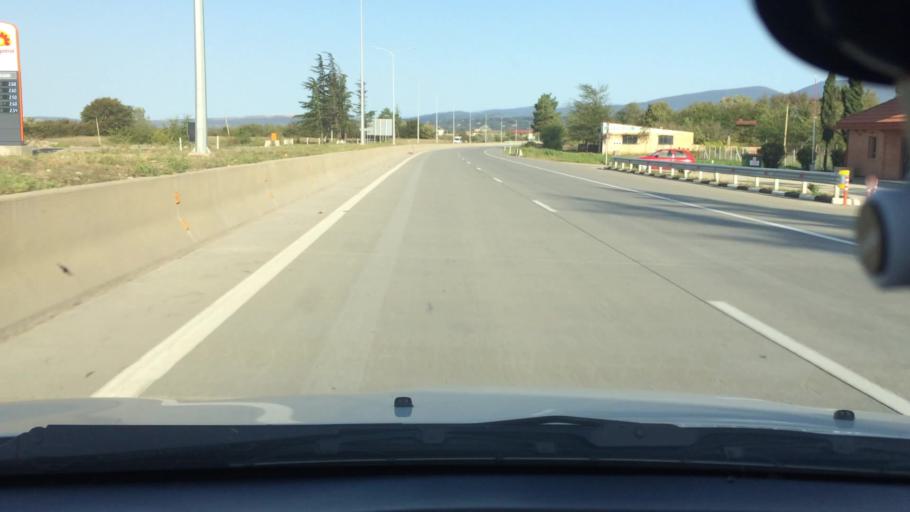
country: GE
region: Imereti
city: Zestap'oni
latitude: 42.1652
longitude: 42.9410
